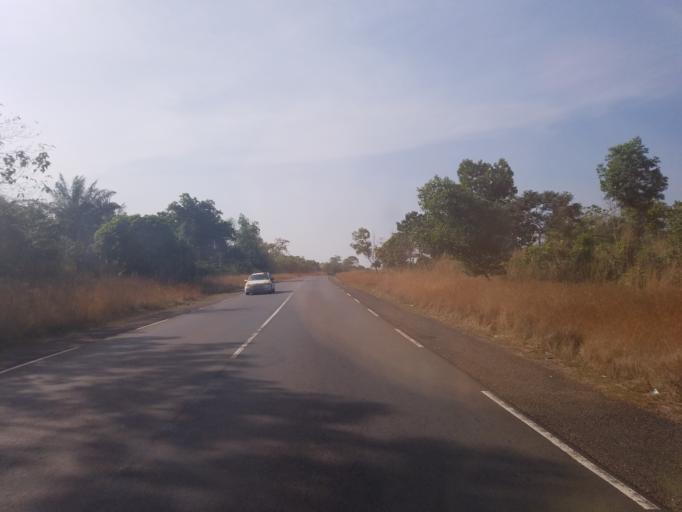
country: GN
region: Boke
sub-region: Boffa
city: Boffa
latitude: 10.1928
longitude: -14.0558
